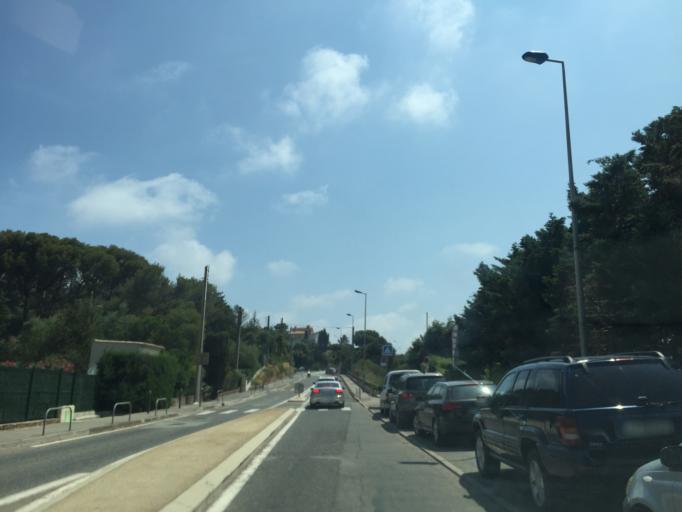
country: FR
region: Provence-Alpes-Cote d'Azur
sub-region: Departement du Var
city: Saint-Raphael
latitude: 43.4300
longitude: 6.8711
